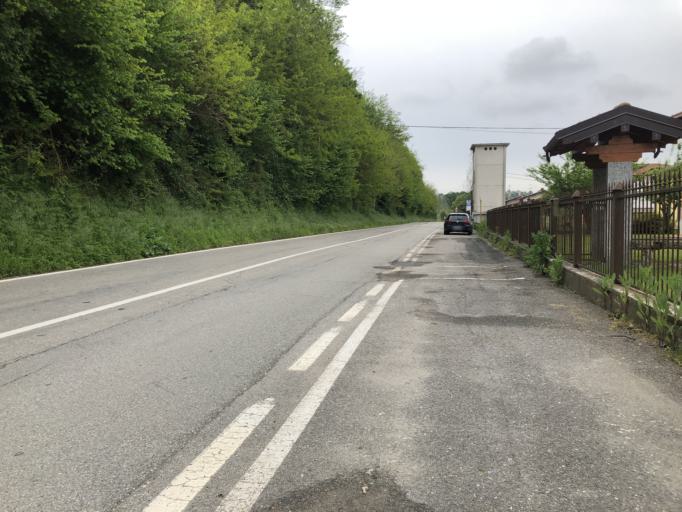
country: IT
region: Piedmont
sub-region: Provincia di Novara
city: Oleggio Castello
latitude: 45.7463
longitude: 8.5289
